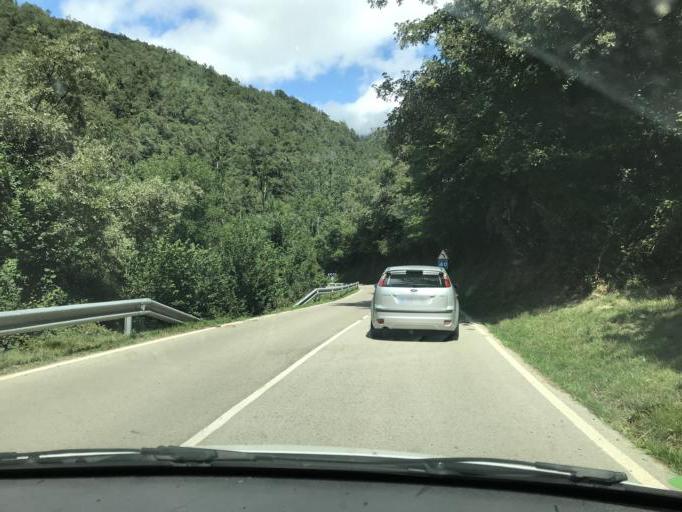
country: ES
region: Cantabria
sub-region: Provincia de Cantabria
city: Cabezon de Liebana
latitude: 43.0773
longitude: -4.4874
